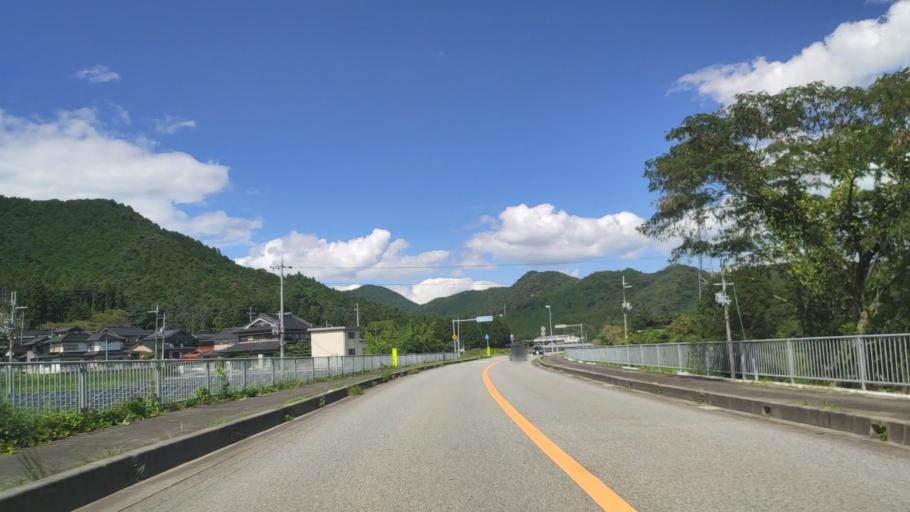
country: JP
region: Kyoto
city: Fukuchiyama
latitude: 35.2392
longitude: 135.1236
